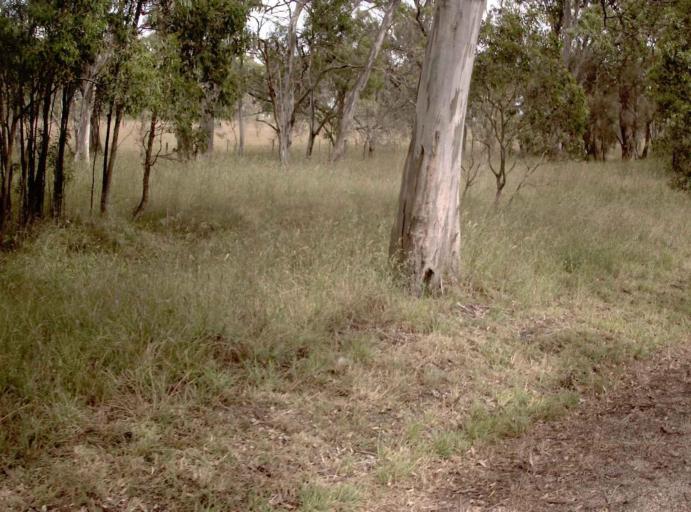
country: AU
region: Victoria
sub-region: Wellington
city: Sale
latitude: -37.9102
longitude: 147.0802
